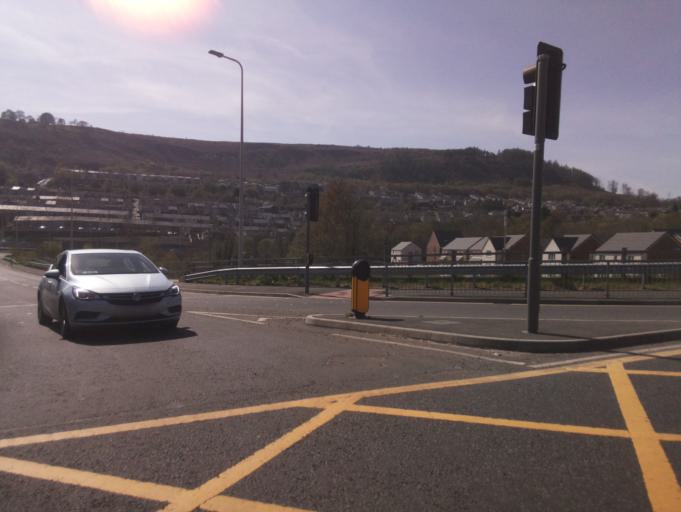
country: GB
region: Wales
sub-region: Rhondda Cynon Taf
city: Mountain Ash
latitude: 51.6782
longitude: -3.3699
